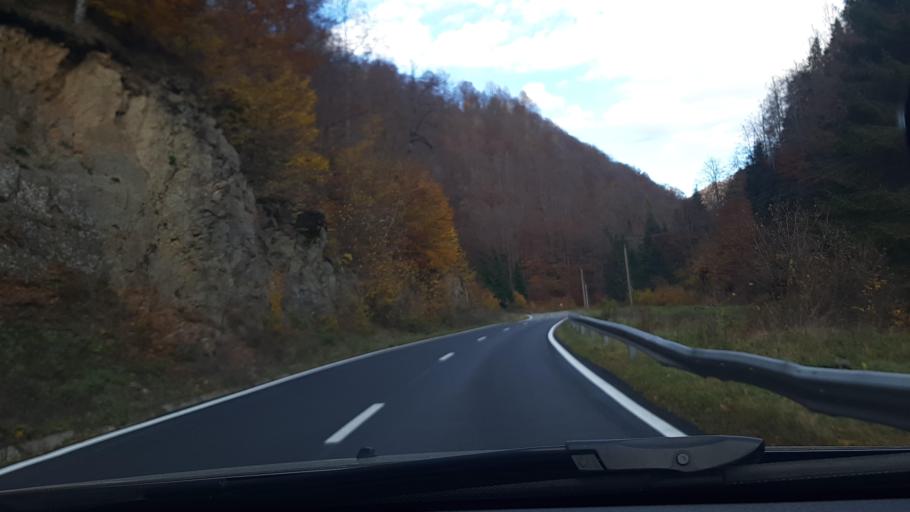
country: RO
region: Valcea
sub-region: Comuna Voineasa
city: Voineasa
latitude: 45.4251
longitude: 23.9202
